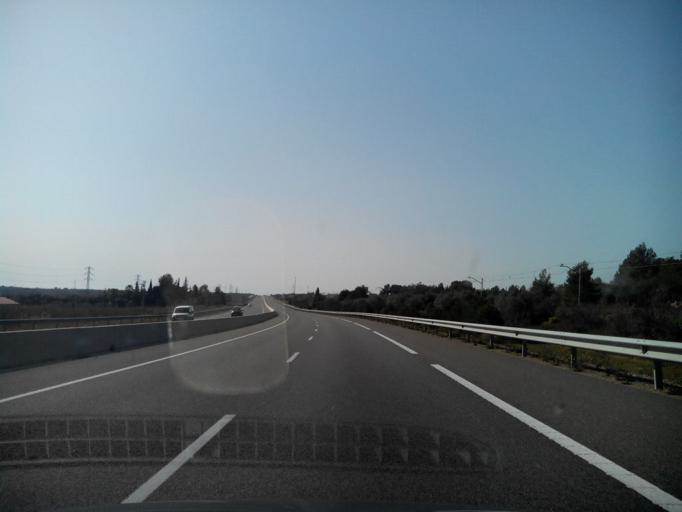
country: ES
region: Catalonia
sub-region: Provincia de Tarragona
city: Alcover
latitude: 41.2434
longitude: 1.1685
